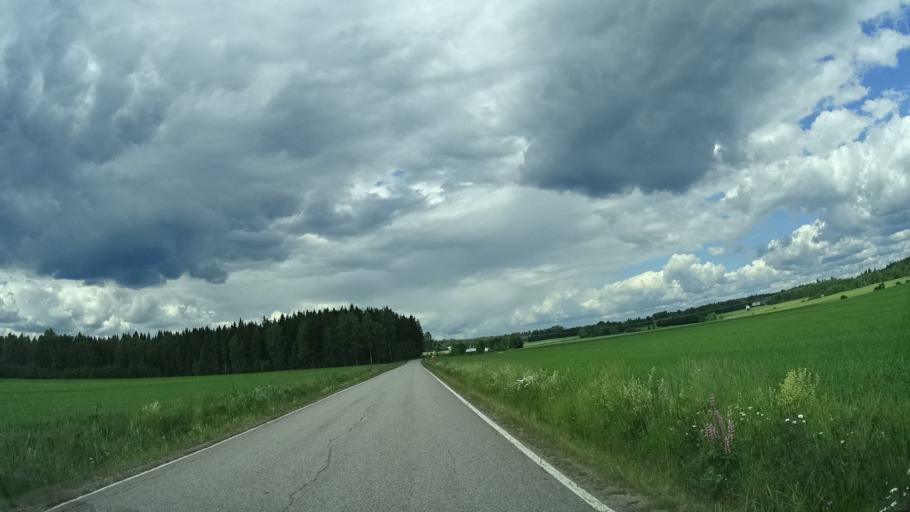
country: FI
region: Uusimaa
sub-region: Helsinki
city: Vihti
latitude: 60.4201
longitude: 24.5387
